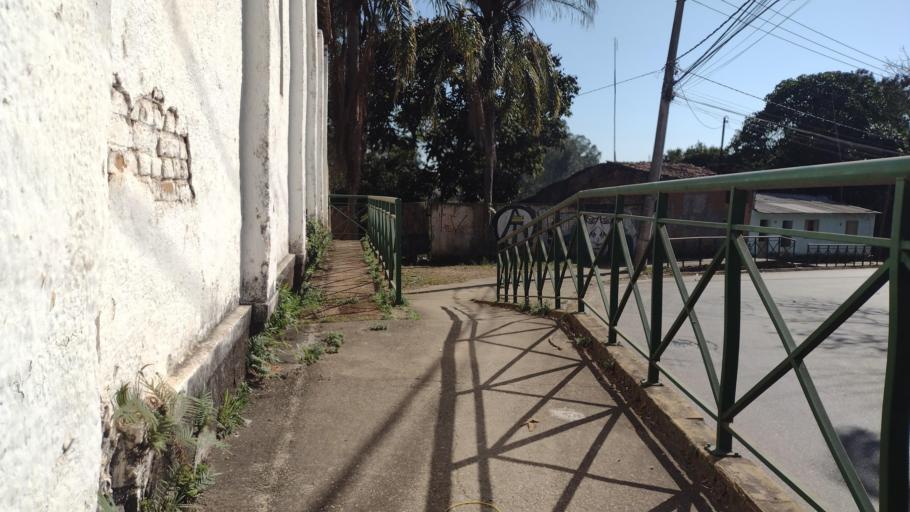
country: BR
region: Sao Paulo
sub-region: Sorocaba
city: Sorocaba
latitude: -23.4106
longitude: -47.4785
